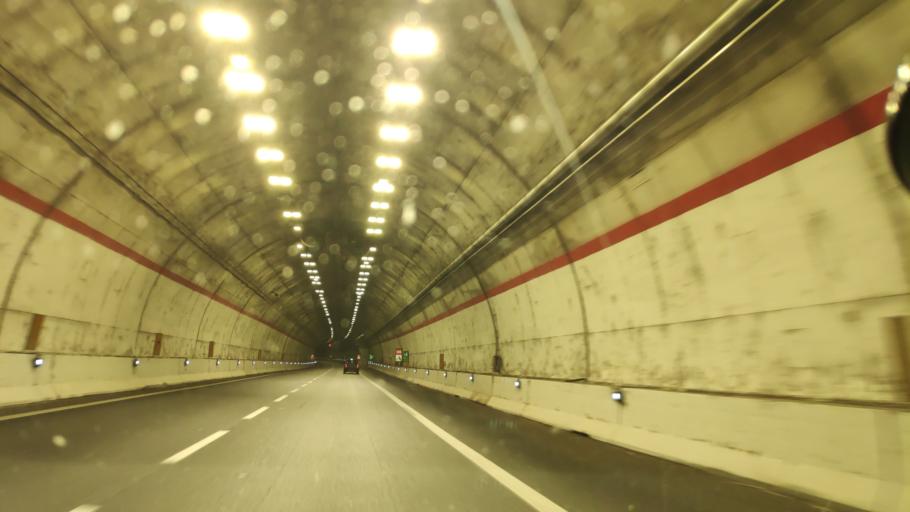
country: IT
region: Campania
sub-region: Provincia di Salerno
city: Sicignano degli Alburni
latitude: 40.6044
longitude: 15.3012
